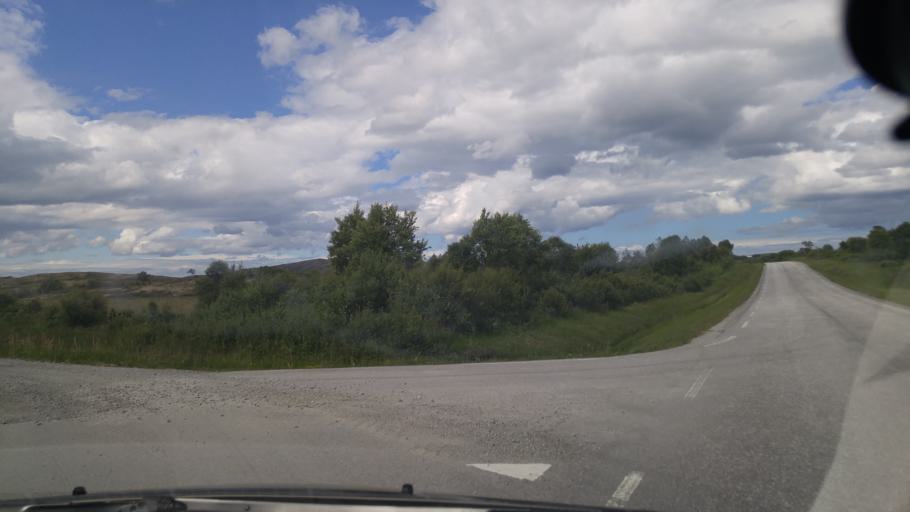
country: NO
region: Nord-Trondelag
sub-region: Vikna
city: Rorvik
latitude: 64.9074
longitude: 11.1353
